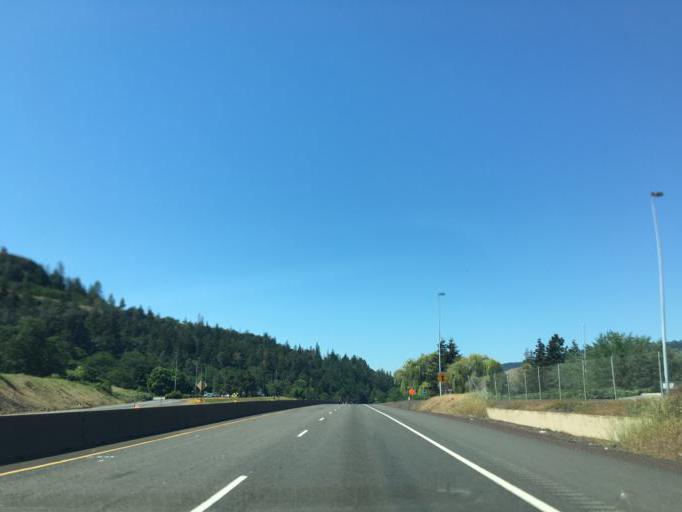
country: US
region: Oregon
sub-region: Wasco County
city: Chenoweth
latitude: 45.6953
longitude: -121.3389
